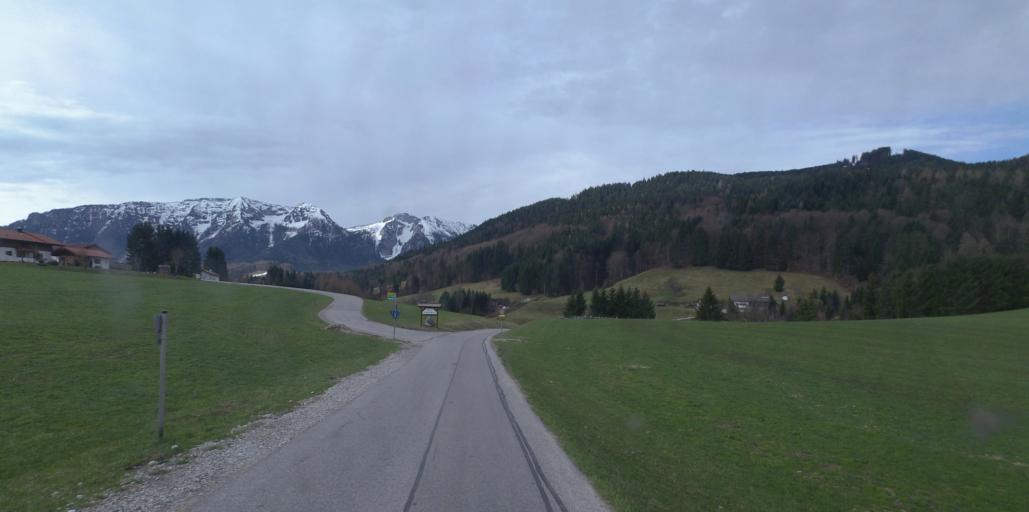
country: DE
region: Bavaria
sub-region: Upper Bavaria
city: Inzell
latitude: 47.7797
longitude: 12.7252
